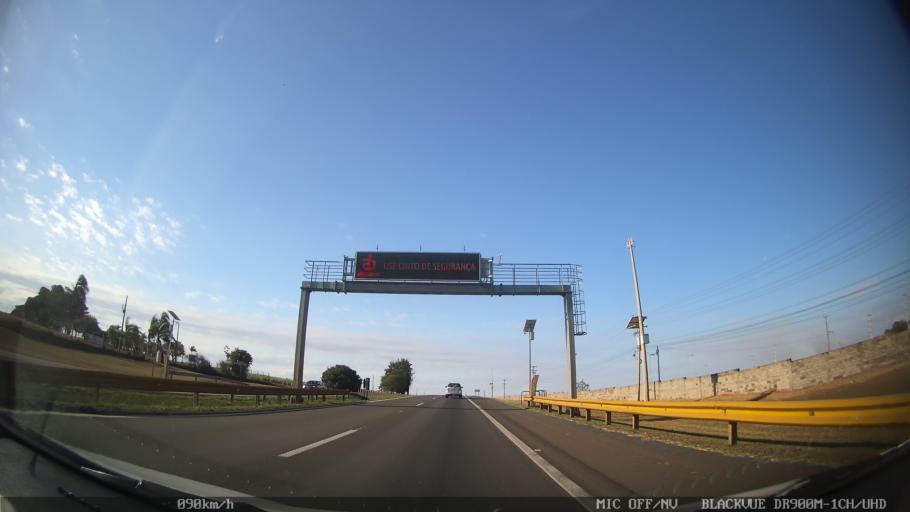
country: BR
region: Sao Paulo
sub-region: Piracicaba
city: Piracicaba
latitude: -22.6907
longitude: -47.6443
